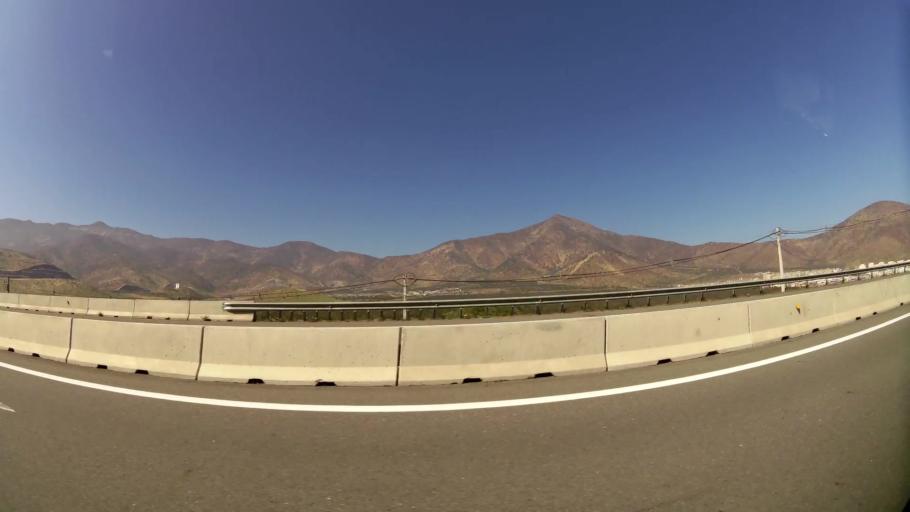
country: CL
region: Santiago Metropolitan
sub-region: Provincia de Chacabuco
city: Chicureo Abajo
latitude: -33.3138
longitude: -70.6389
